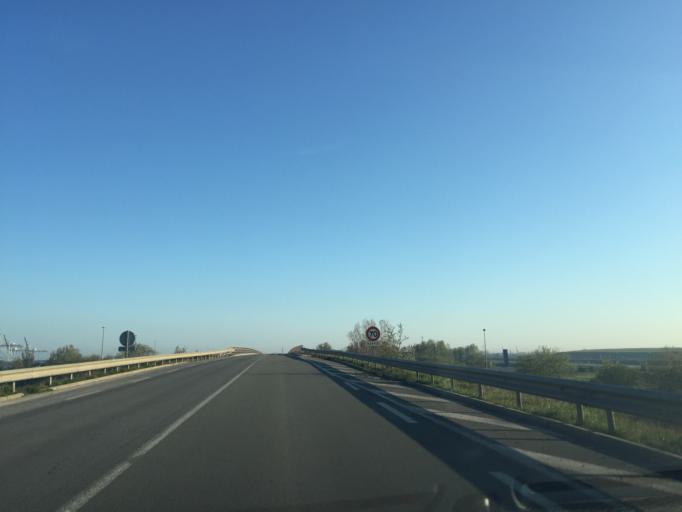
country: FR
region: Nord-Pas-de-Calais
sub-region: Departement du Nord
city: Loon-Plage
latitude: 50.9942
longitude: 2.1980
